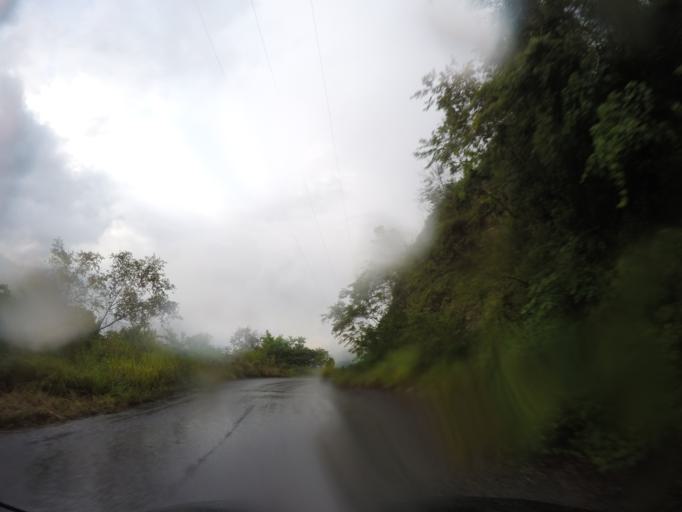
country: MX
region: Oaxaca
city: San Gabriel Mixtepec
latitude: 16.0630
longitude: -97.0757
